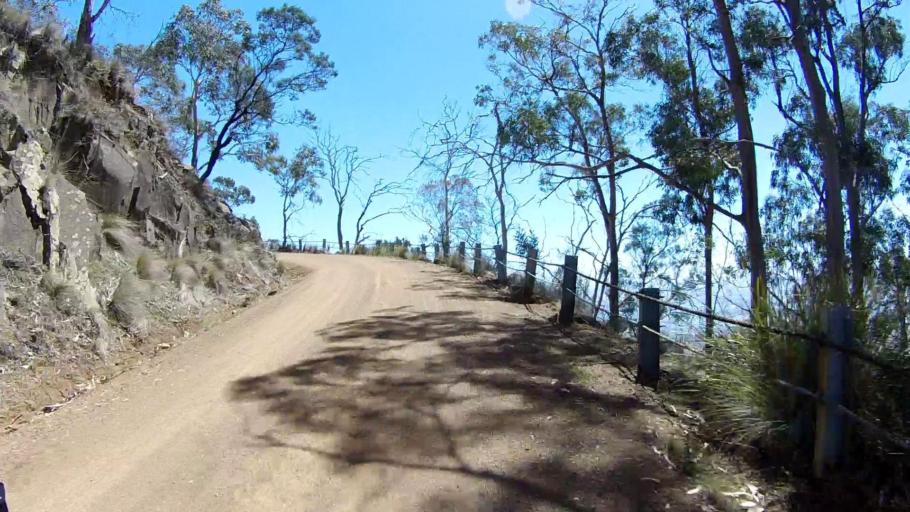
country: AU
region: Tasmania
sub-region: Clarence
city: Cambridge
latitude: -42.8612
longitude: 147.4550
